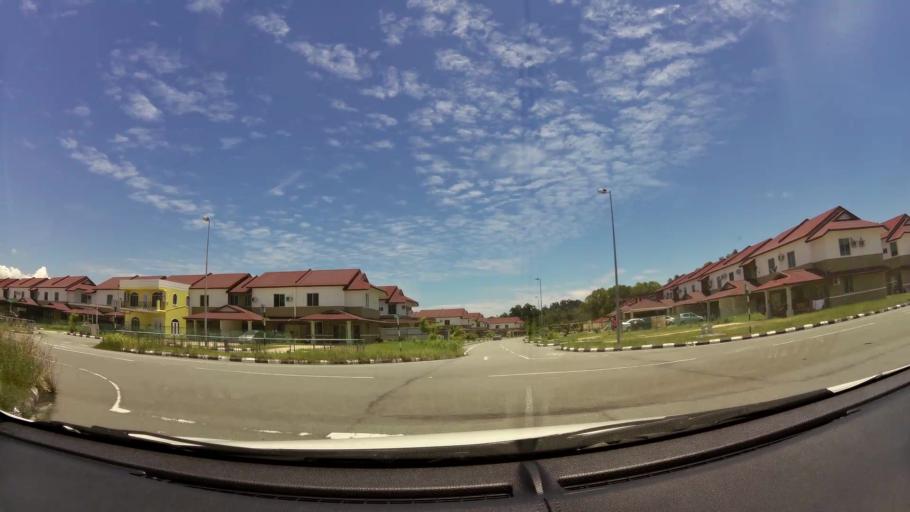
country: BN
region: Brunei and Muara
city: Bandar Seri Begawan
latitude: 5.0077
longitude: 115.0058
